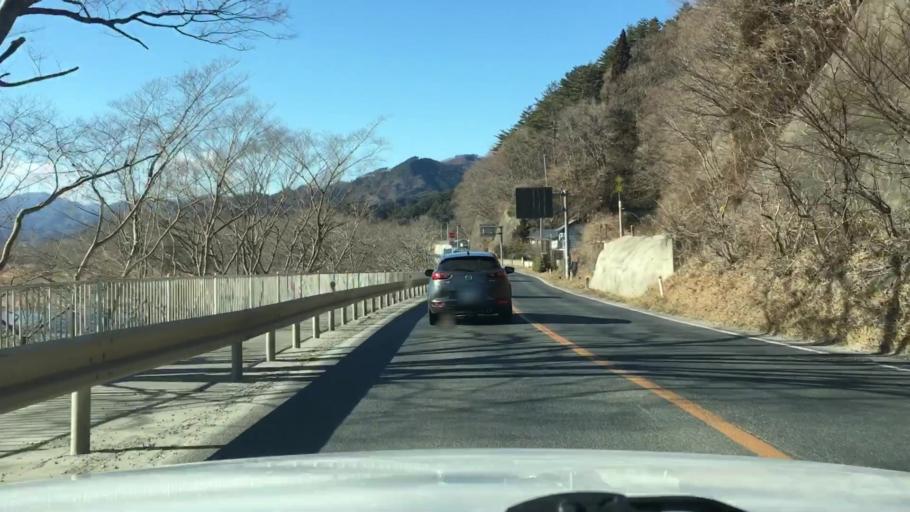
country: JP
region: Iwate
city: Miyako
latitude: 39.6315
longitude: 141.9054
